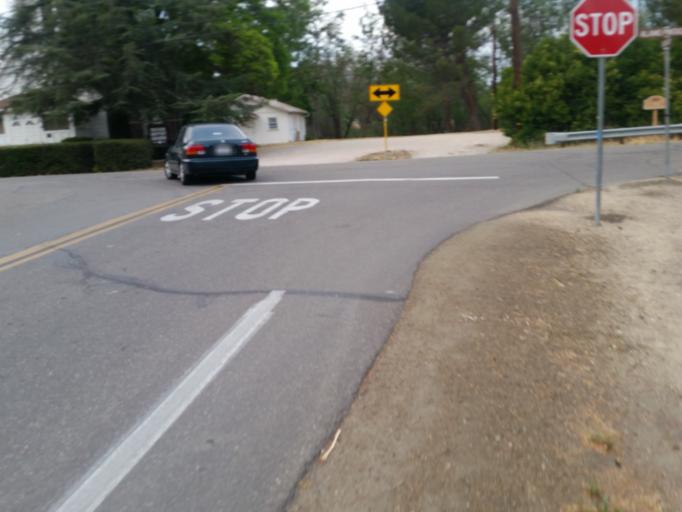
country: US
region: California
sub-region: Santa Barbara County
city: Los Olivos
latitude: 34.6654
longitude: -120.1182
